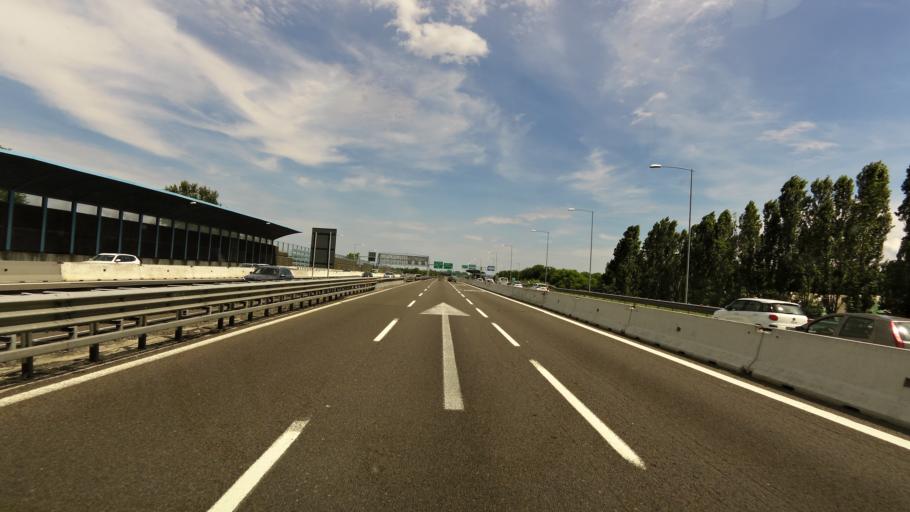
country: IT
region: Emilia-Romagna
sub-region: Provincia di Bologna
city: Bologna
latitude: 44.5284
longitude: 11.3496
